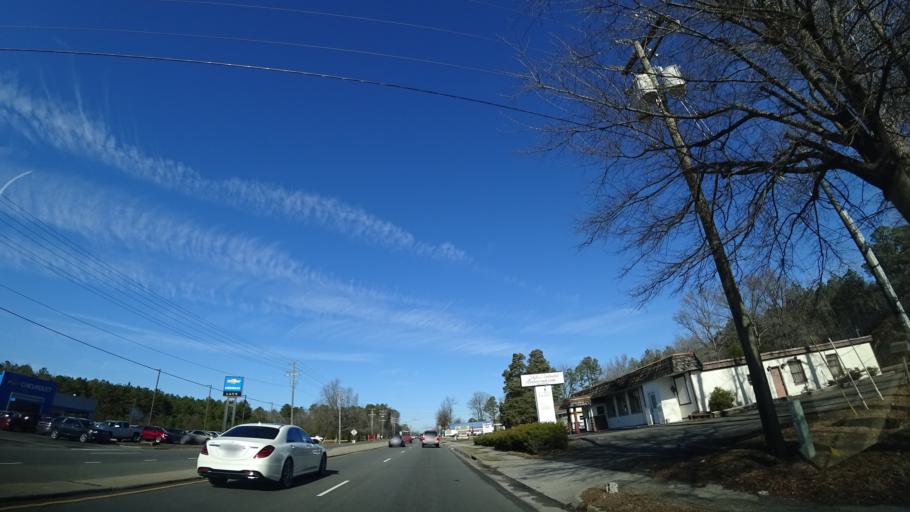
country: US
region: Virginia
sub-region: Hanover County
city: Ashland
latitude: 37.7465
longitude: -77.4712
